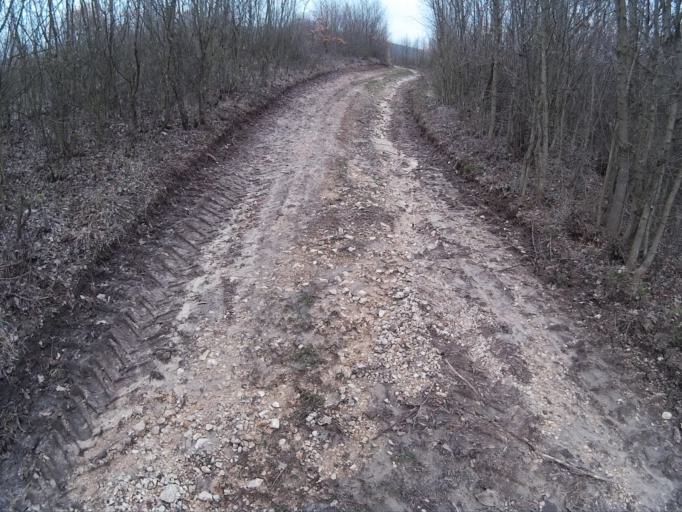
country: HU
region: Veszprem
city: Veszprem
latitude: 47.1687
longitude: 17.8698
